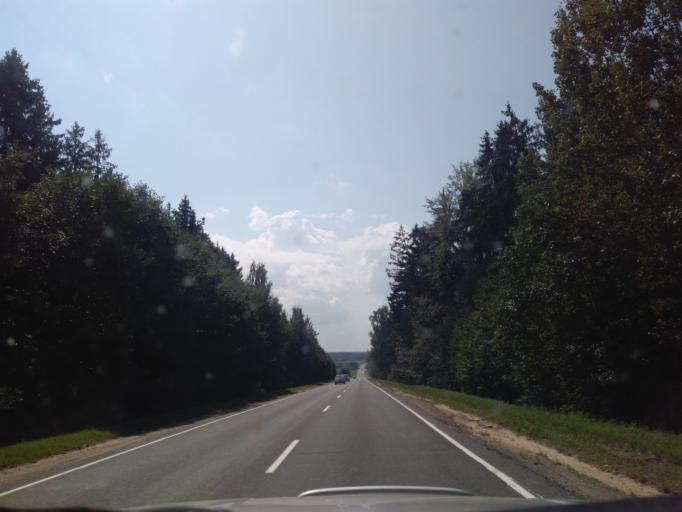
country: BY
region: Minsk
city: Khatsyezhyna
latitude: 53.8967
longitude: 27.2577
